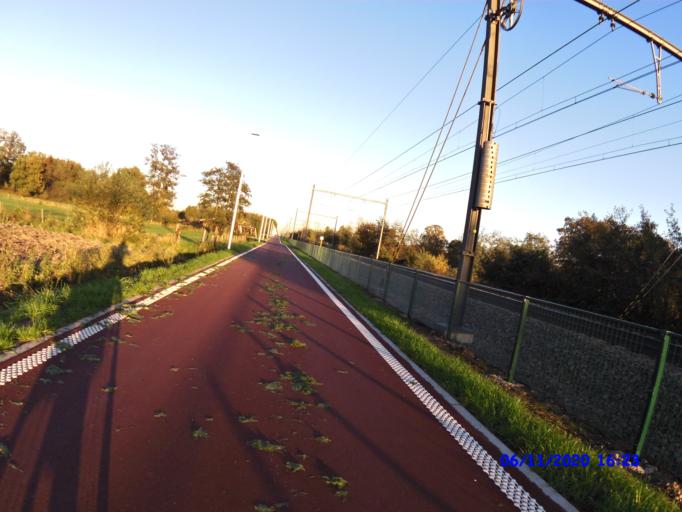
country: BE
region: Flanders
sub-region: Provincie Antwerpen
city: Meerhout
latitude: 51.1797
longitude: 5.0523
